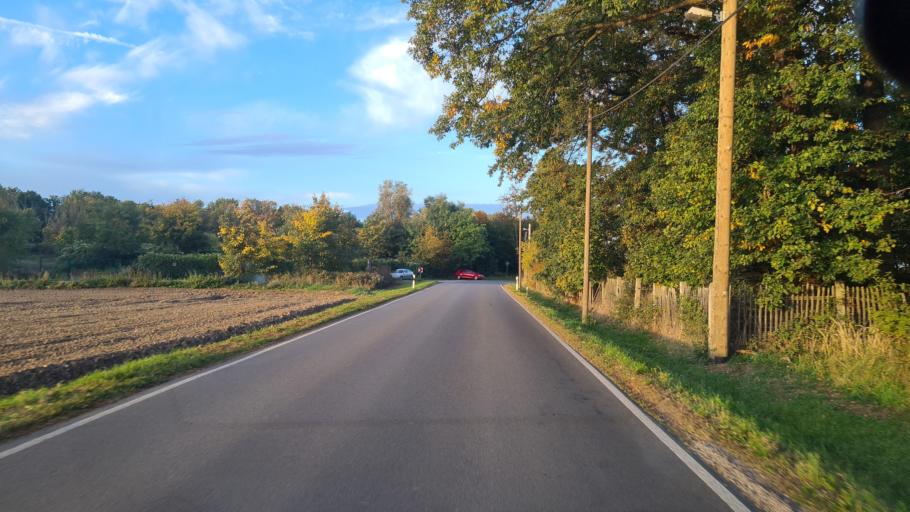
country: DE
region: Saxony
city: Machern
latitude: 51.3654
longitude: 12.6378
